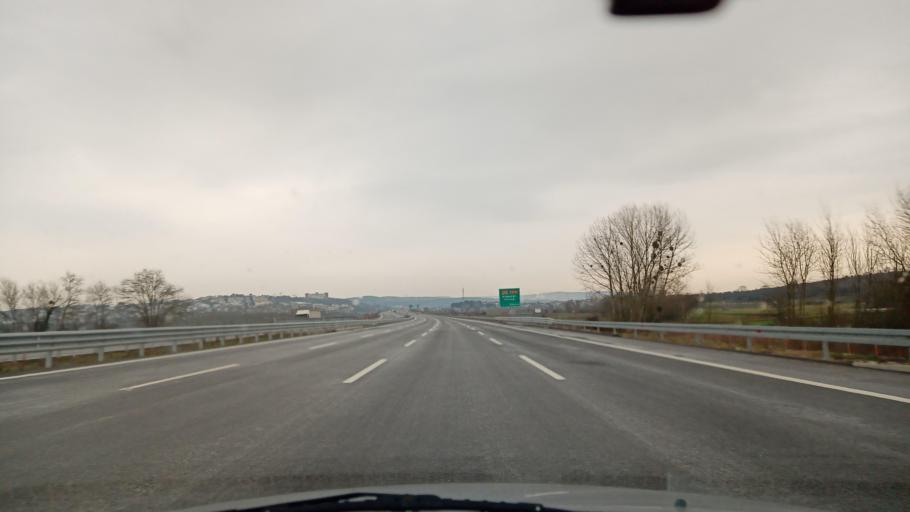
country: TR
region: Sakarya
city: Kazimpasa
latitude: 40.8431
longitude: 30.3092
